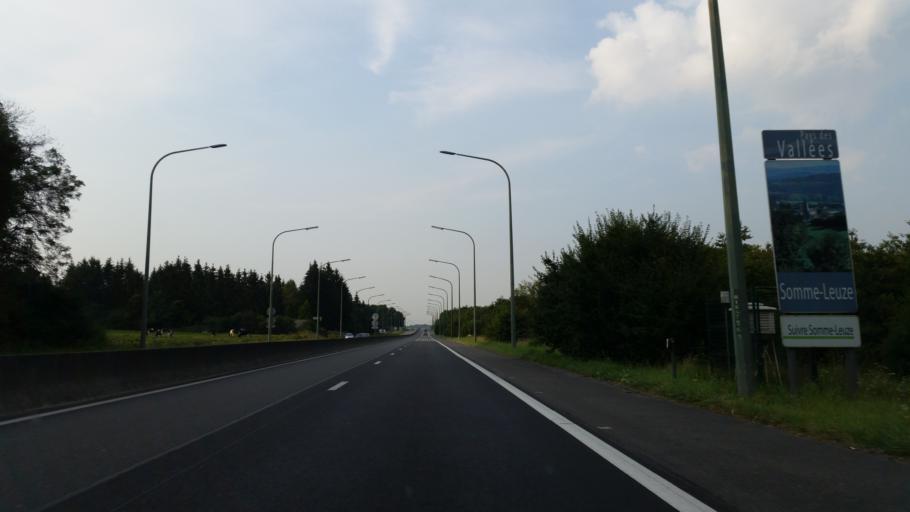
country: BE
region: Wallonia
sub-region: Province du Luxembourg
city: Marche-en-Famenne
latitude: 50.2707
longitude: 5.3476
